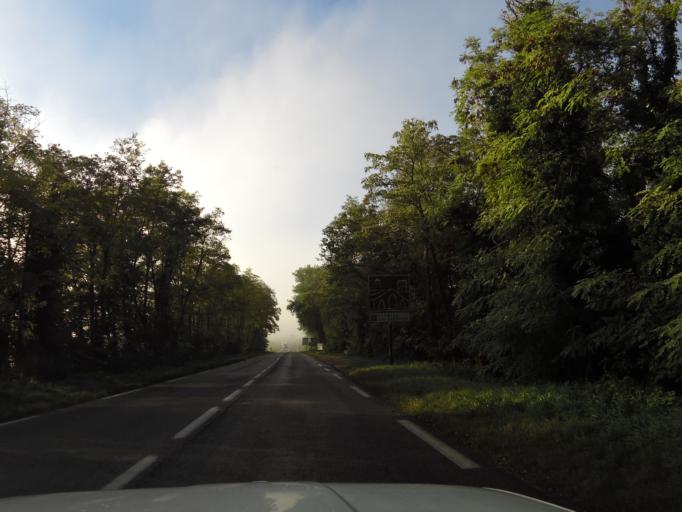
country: FR
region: Rhone-Alpes
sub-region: Departement de l'Ain
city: Lagnieu
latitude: 45.8819
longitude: 5.3476
